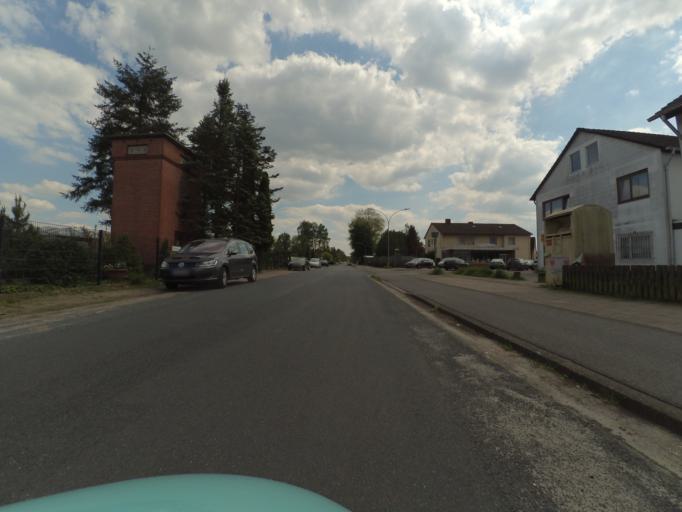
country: DE
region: Lower Saxony
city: Winsen
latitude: 52.6417
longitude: 9.9348
